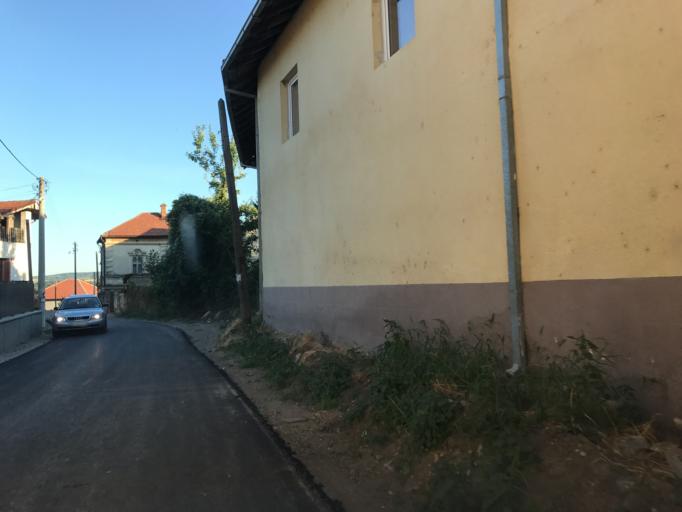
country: BG
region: Vidin
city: Bregovo
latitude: 44.1245
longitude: 22.5982
